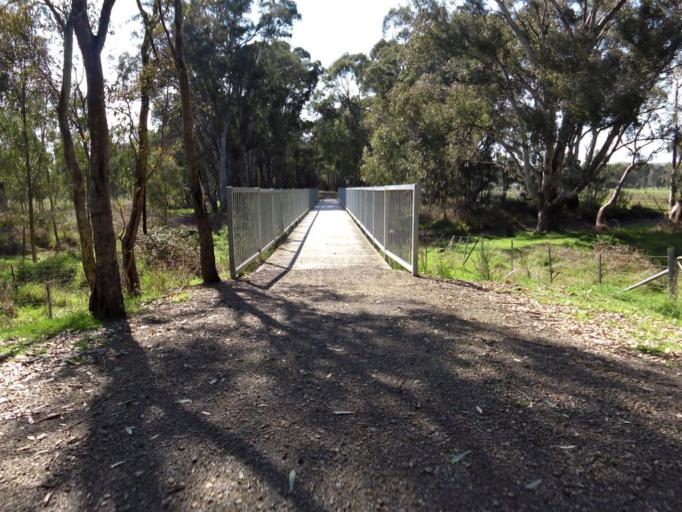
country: AU
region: Victoria
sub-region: Murrindindi
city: Alexandra
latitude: -37.1575
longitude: 145.5707
